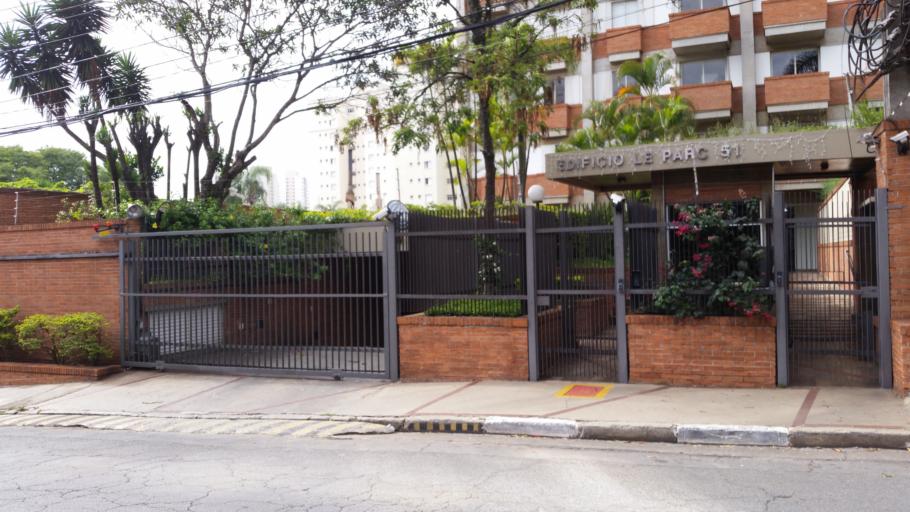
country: BR
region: Sao Paulo
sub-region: Diadema
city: Diadema
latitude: -23.6593
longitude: -46.6922
